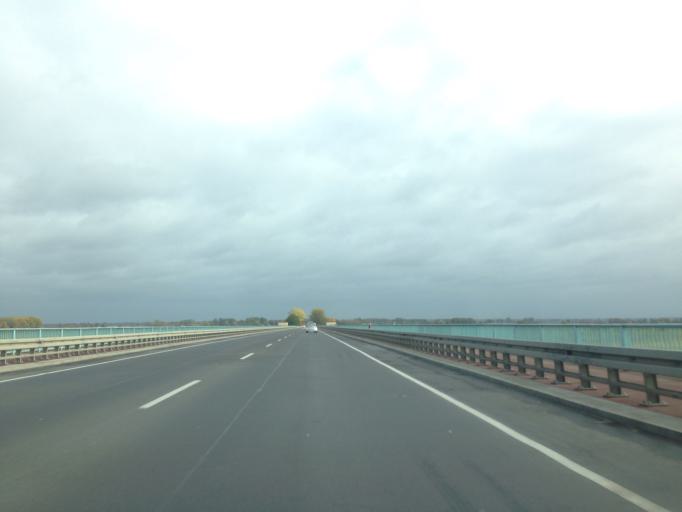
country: PL
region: Pomeranian Voivodeship
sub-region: Powiat malborski
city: Lisewo Malborskie
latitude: 54.0522
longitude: 18.8194
